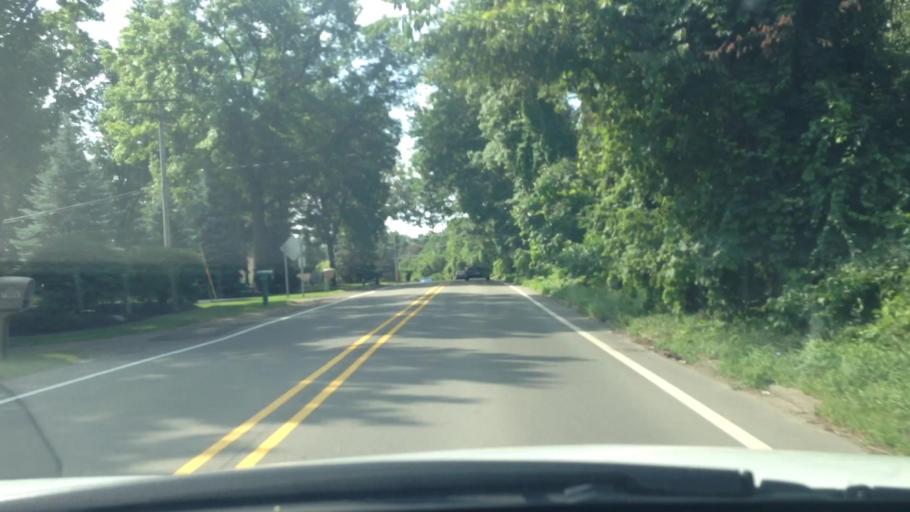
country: US
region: Michigan
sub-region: Oakland County
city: Waterford
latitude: 42.6859
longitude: -83.4340
